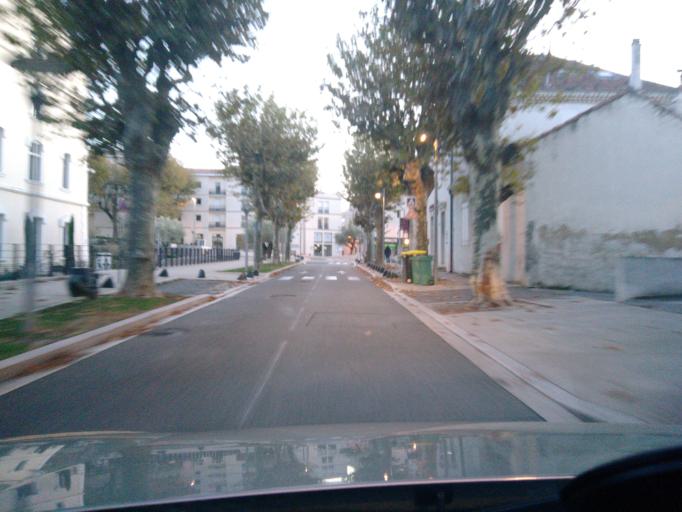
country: FR
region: Rhone-Alpes
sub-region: Departement de la Drome
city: Montelimar
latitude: 44.5621
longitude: 4.7516
